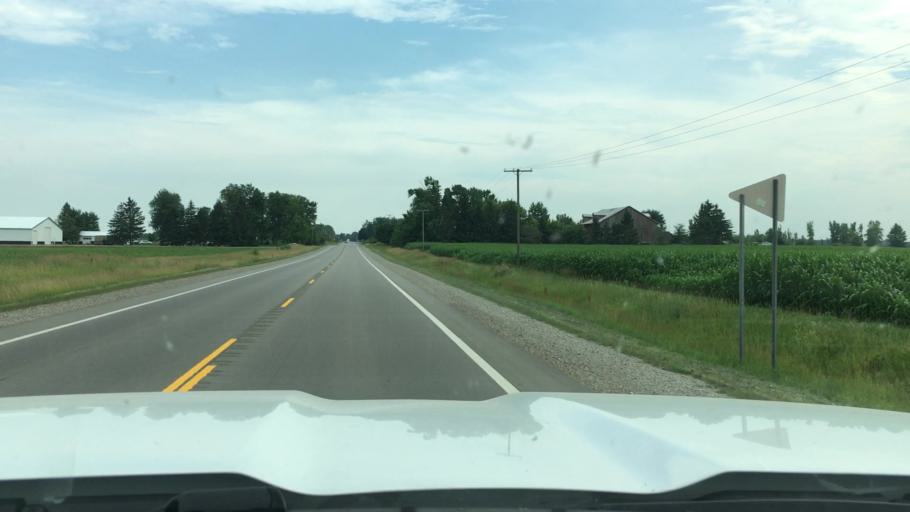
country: US
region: Michigan
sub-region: Sanilac County
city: Marlette
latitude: 43.3543
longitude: -83.0849
